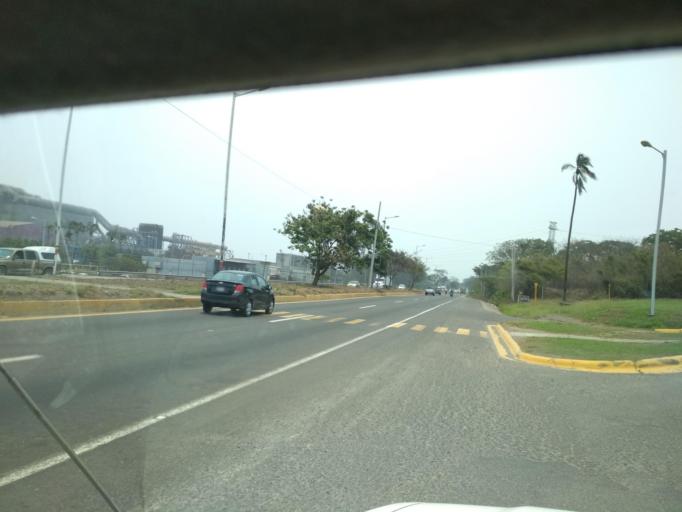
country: MX
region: Veracruz
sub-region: Veracruz
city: Oasis
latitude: 19.1773
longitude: -96.2448
